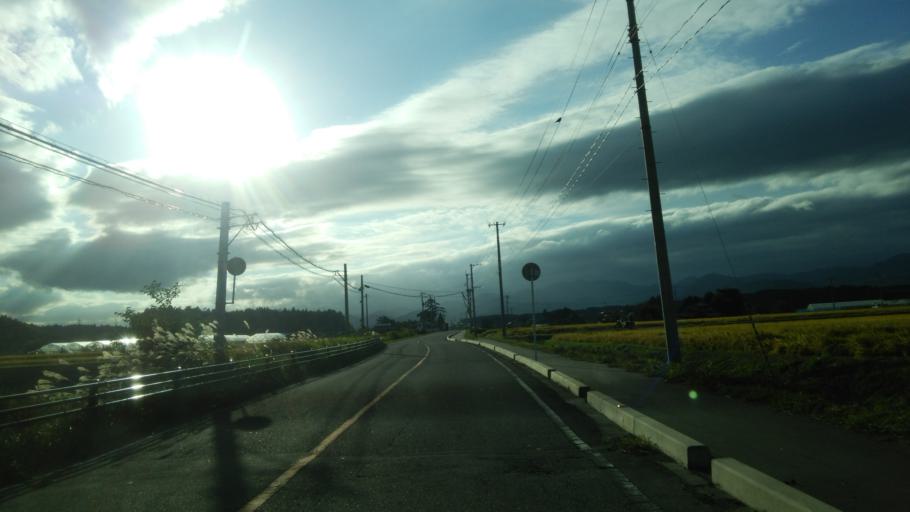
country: JP
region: Fukushima
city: Sukagawa
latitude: 37.3314
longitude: 140.3115
